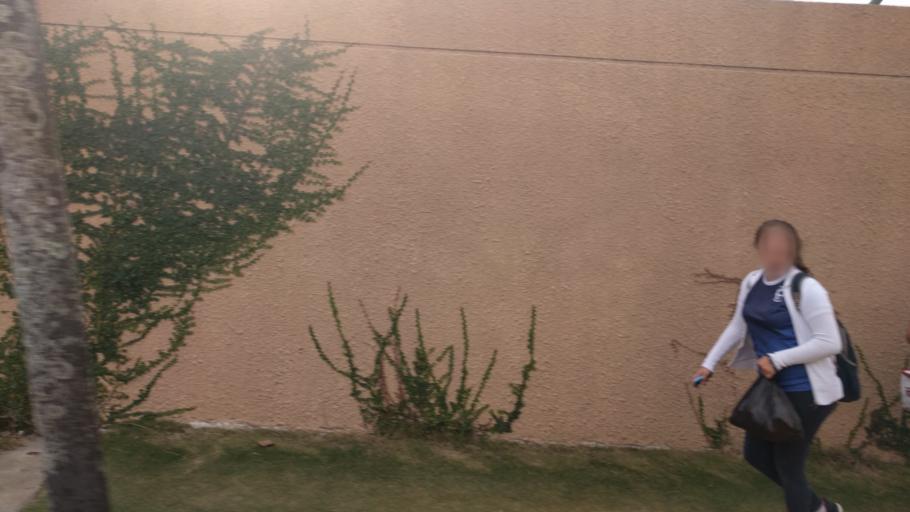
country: BO
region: Santa Cruz
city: Santa Cruz de la Sierra
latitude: -17.8030
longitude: -63.2055
